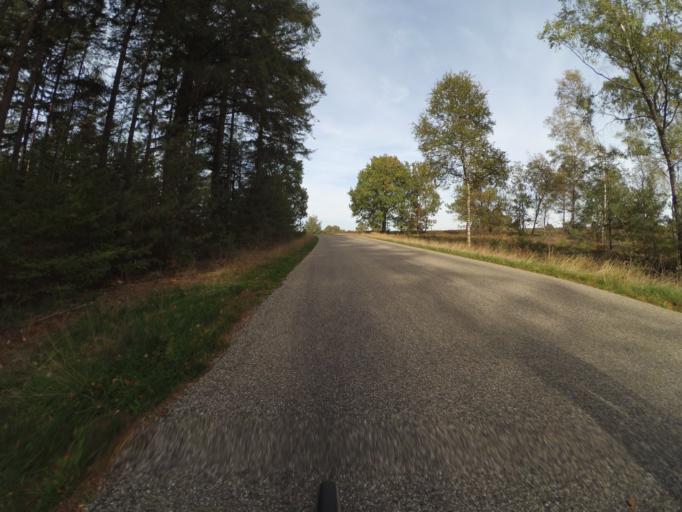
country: NL
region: Overijssel
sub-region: Gemeente Hof van Twente
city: Markelo
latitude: 52.3173
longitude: 6.4133
